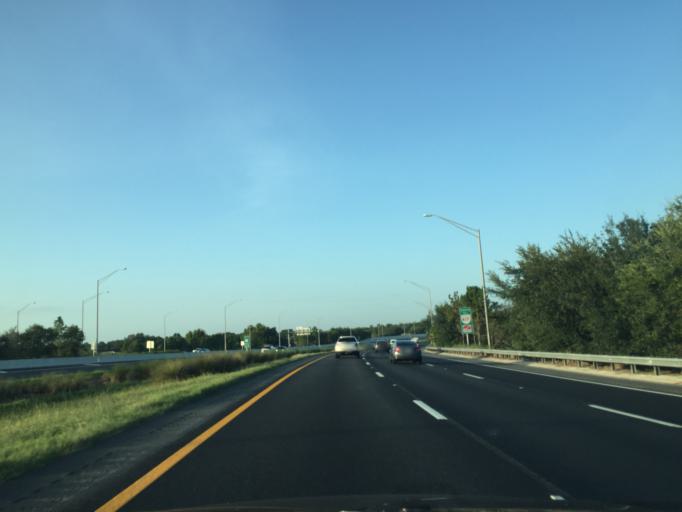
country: US
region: Florida
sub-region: Seminole County
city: Goldenrod
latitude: 28.5968
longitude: -81.2501
